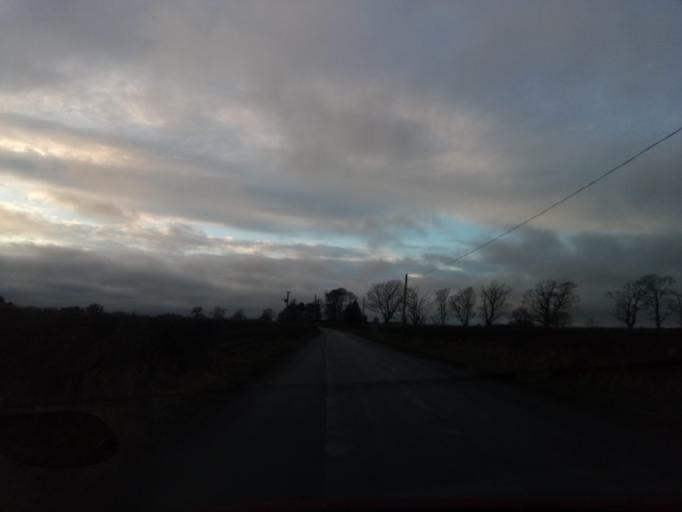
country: GB
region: England
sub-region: Northumberland
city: Meldon
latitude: 55.1329
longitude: -1.7763
